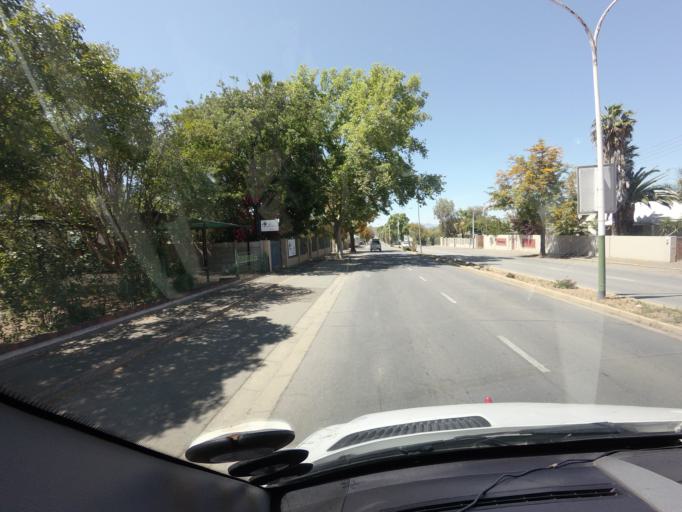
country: ZA
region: Western Cape
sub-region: Eden District Municipality
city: Oudtshoorn
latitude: -33.6041
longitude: 22.2095
